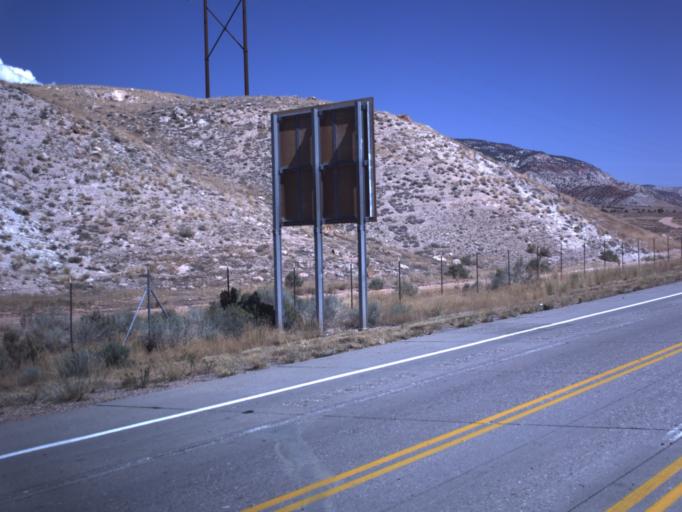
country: US
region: Utah
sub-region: Sevier County
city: Richfield
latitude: 38.8036
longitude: -112.0653
